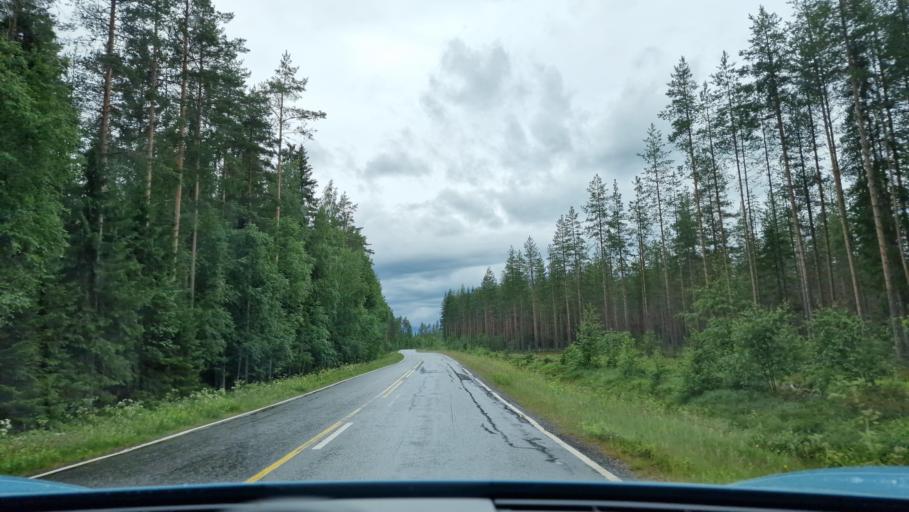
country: FI
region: Central Finland
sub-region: Saarijaervi-Viitasaari
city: Pylkoenmaeki
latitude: 62.6693
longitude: 24.5248
